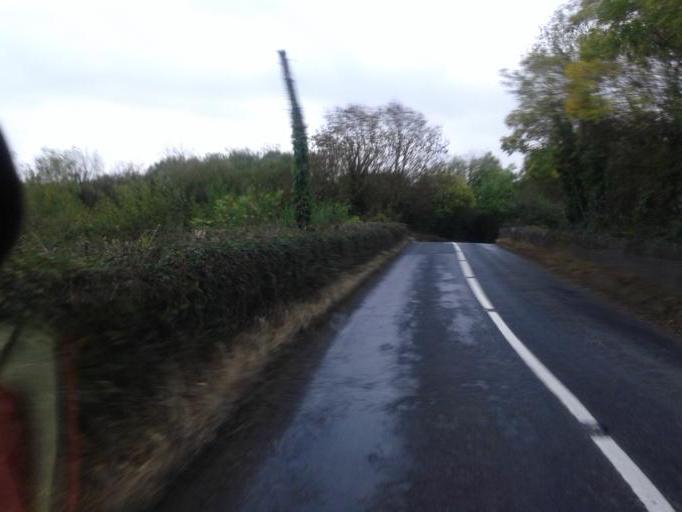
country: IE
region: Munster
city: Ballina
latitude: 52.7730
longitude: -8.4305
